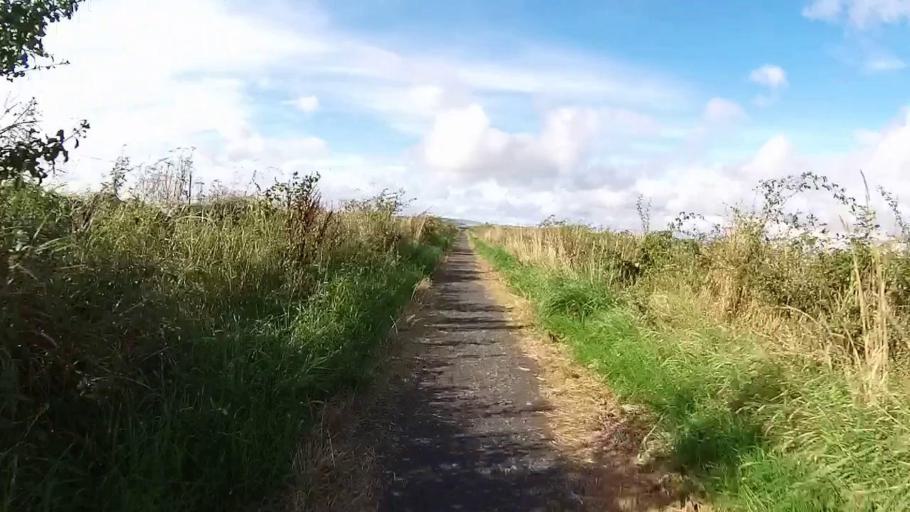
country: GB
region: Scotland
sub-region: Fife
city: Kelty
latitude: 56.1759
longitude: -3.3833
